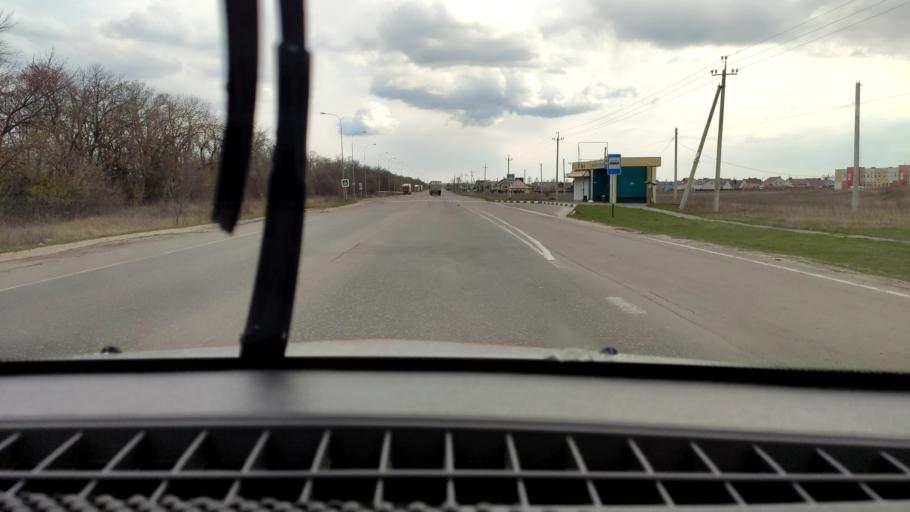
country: RU
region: Voronezj
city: Novaya Usman'
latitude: 51.6239
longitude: 39.3348
